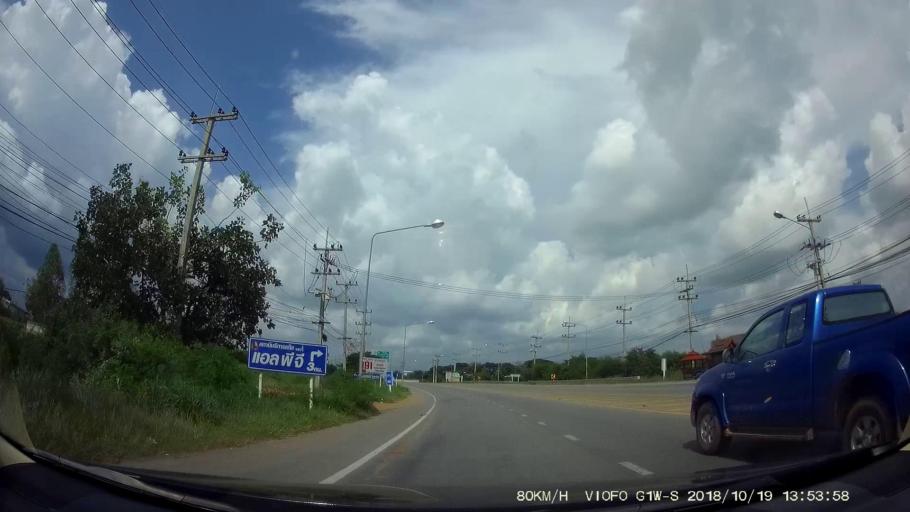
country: TH
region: Chaiyaphum
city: Chaiyaphum
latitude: 15.7825
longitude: 102.0267
